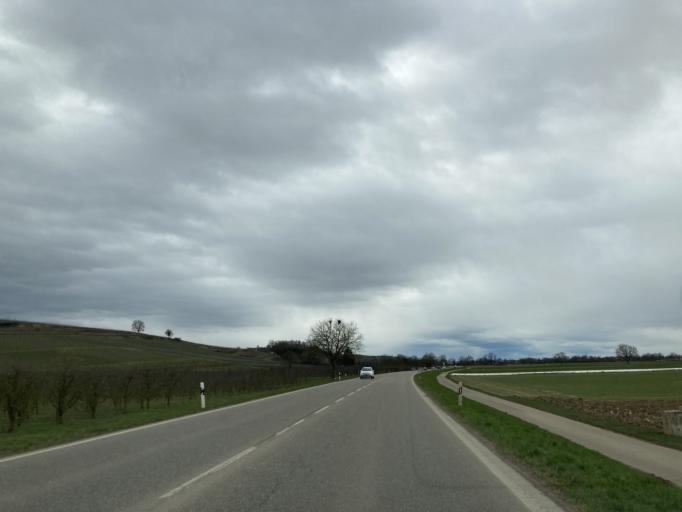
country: DE
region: Baden-Wuerttemberg
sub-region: Freiburg Region
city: Mullheim
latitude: 47.8255
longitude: 7.6196
